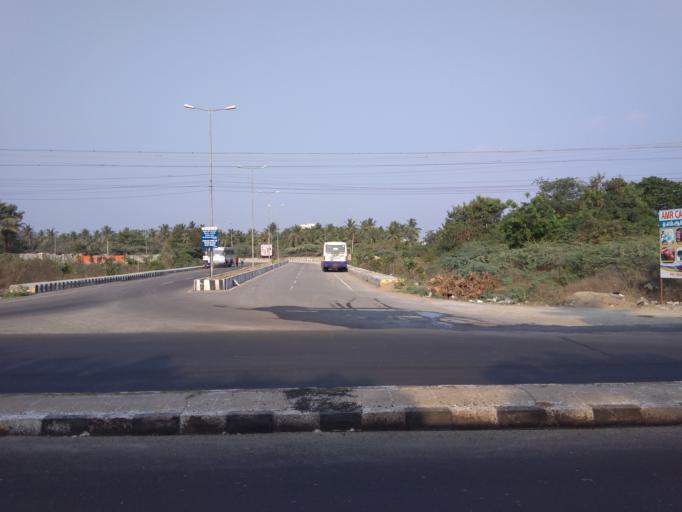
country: IN
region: Tamil Nadu
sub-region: Kancheepuram
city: Injambakkam
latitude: 12.8260
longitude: 80.2314
